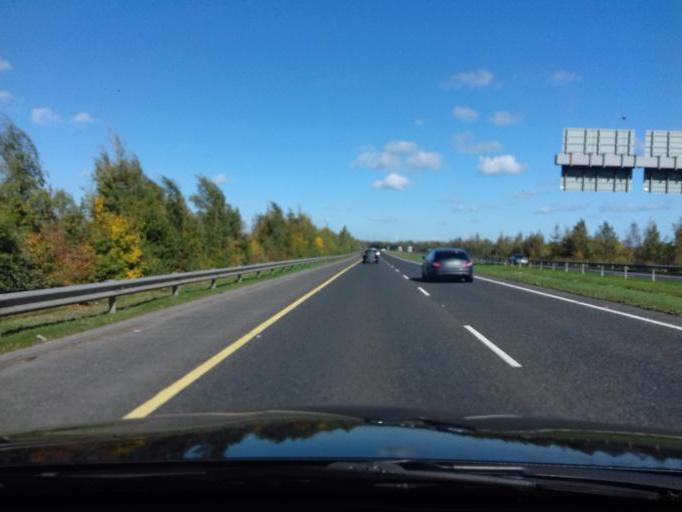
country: IE
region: Leinster
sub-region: Fingal County
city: Blanchardstown
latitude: 53.4478
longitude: -6.3560
